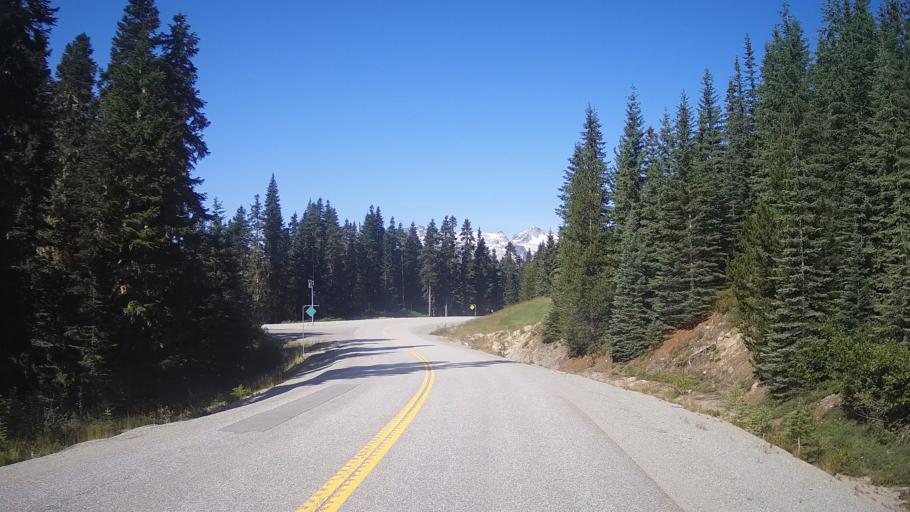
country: CA
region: British Columbia
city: Pemberton
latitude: 50.3811
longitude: -122.4729
